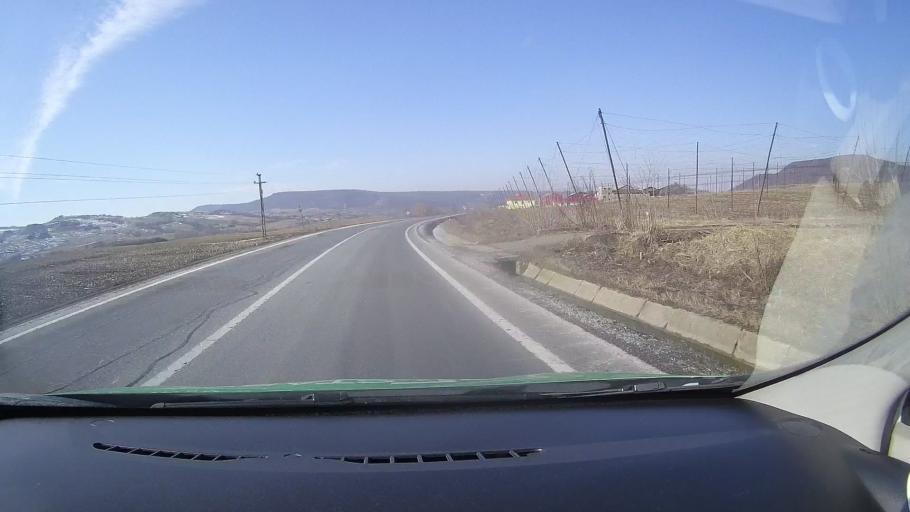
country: RO
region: Mures
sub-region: Comuna Saschiz
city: Saschiz
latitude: 46.1727
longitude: 24.9867
